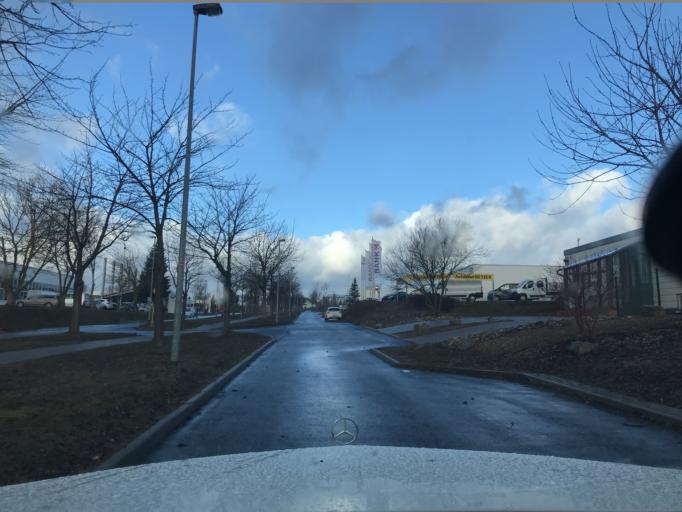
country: DE
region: Thuringia
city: Muehlhausen
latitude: 51.1963
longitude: 10.4761
